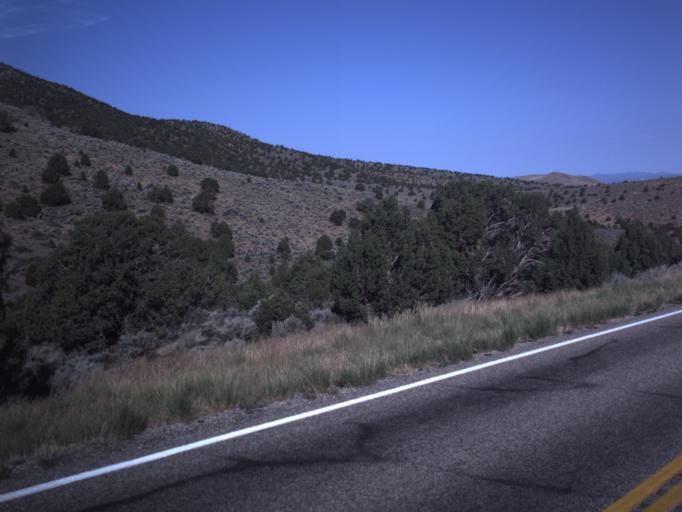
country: US
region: Utah
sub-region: Beaver County
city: Milford
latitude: 38.1234
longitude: -112.9525
